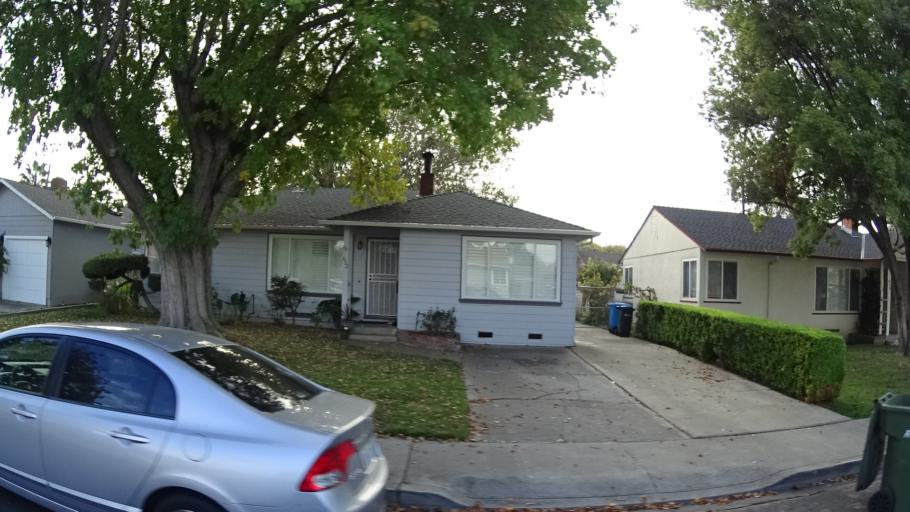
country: US
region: California
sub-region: Santa Clara County
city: Santa Clara
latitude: 37.3387
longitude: -121.9604
